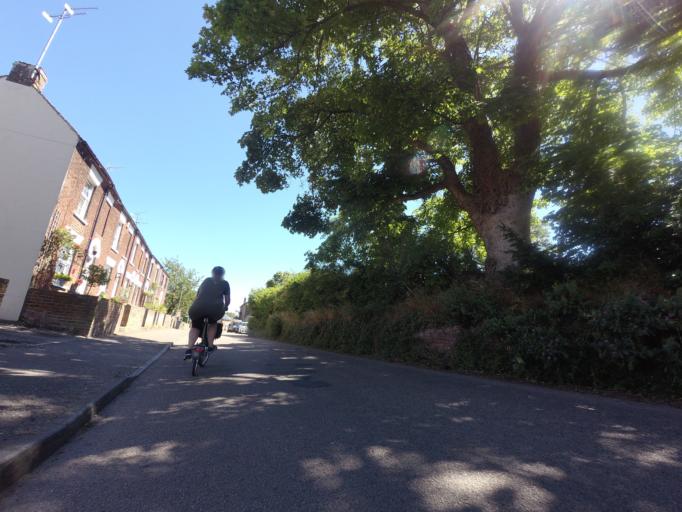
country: GB
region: England
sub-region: Kent
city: Eastry
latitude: 51.2444
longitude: 1.3054
